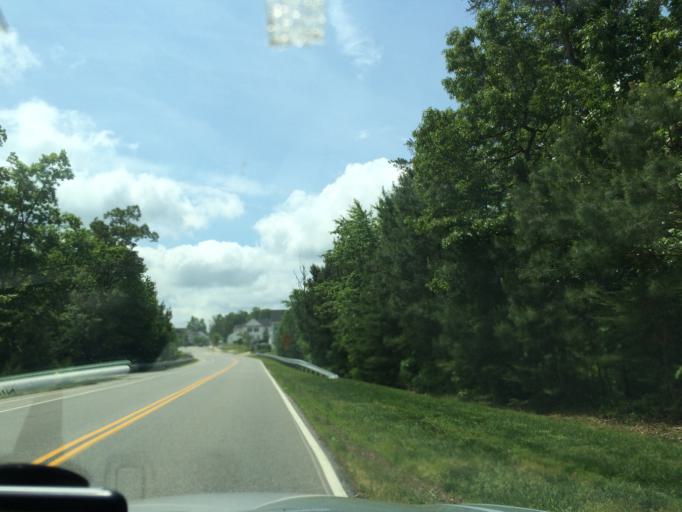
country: US
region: Maryland
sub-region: Saint Mary's County
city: California
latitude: 38.2979
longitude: -76.5469
